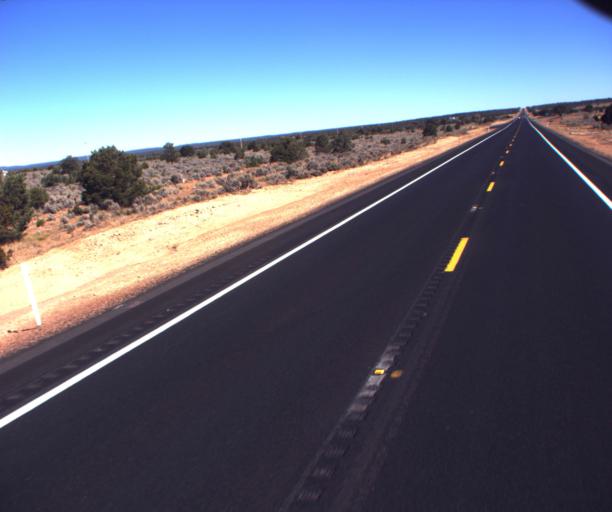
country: US
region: Arizona
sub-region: Apache County
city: Ganado
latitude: 35.7171
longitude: -109.4115
